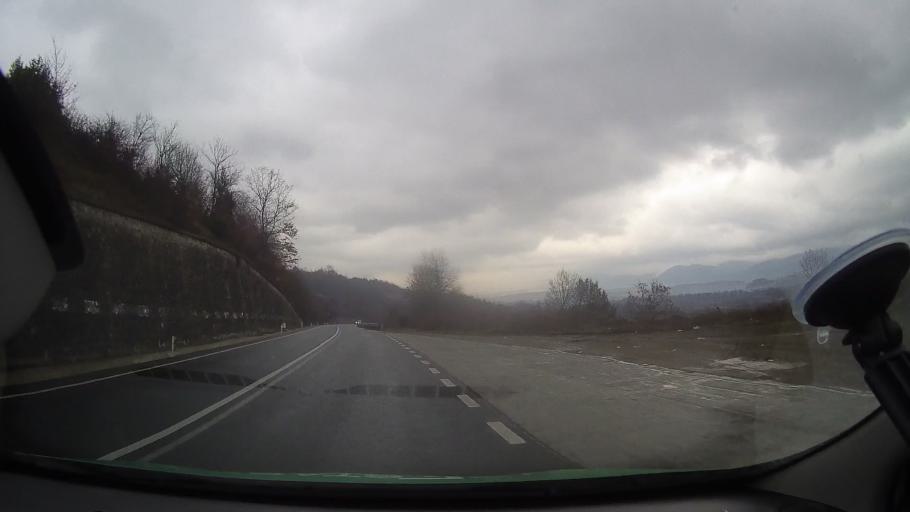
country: RO
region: Hunedoara
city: Vata de Jos
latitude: 46.2069
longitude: 22.5822
